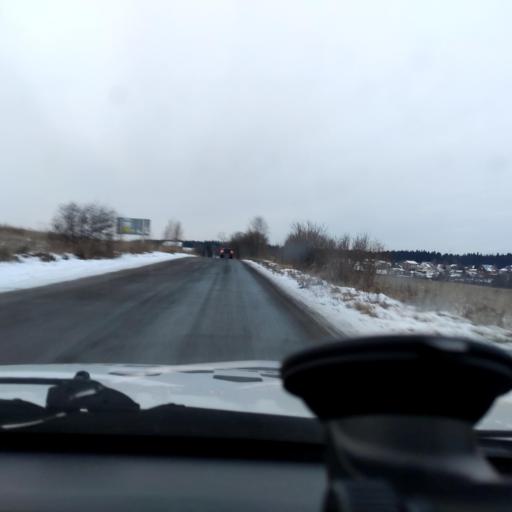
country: RU
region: Perm
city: Ferma
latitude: 57.9322
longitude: 56.3280
